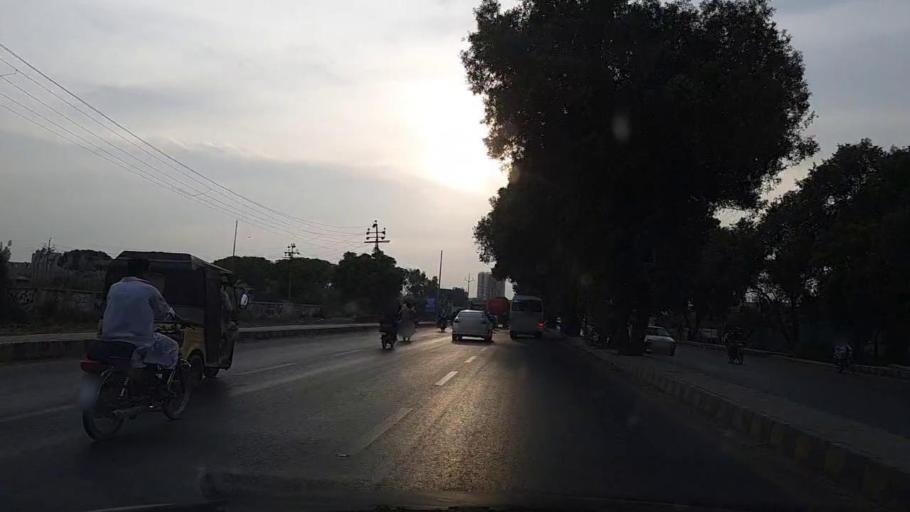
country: PK
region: Sindh
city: Malir Cantonment
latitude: 24.8543
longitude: 67.2522
